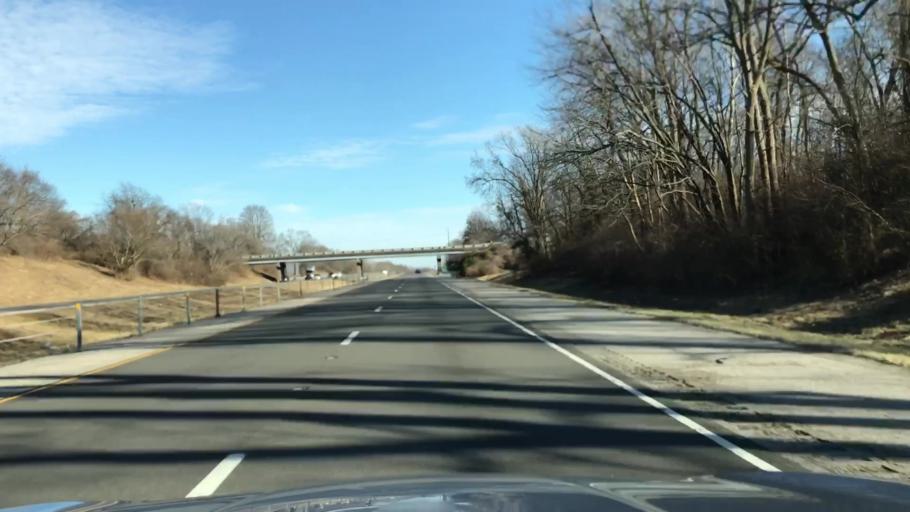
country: US
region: Illinois
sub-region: Madison County
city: Glen Carbon
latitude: 38.7567
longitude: -89.9772
